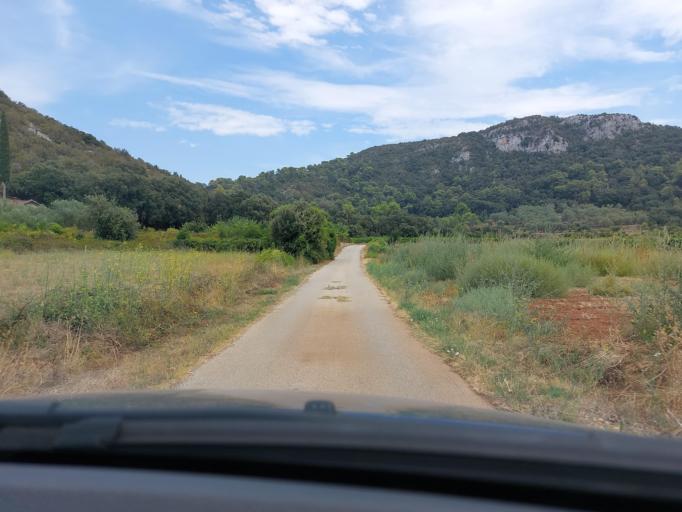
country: HR
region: Dubrovacko-Neretvanska
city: Smokvica
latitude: 42.7554
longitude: 16.9200
